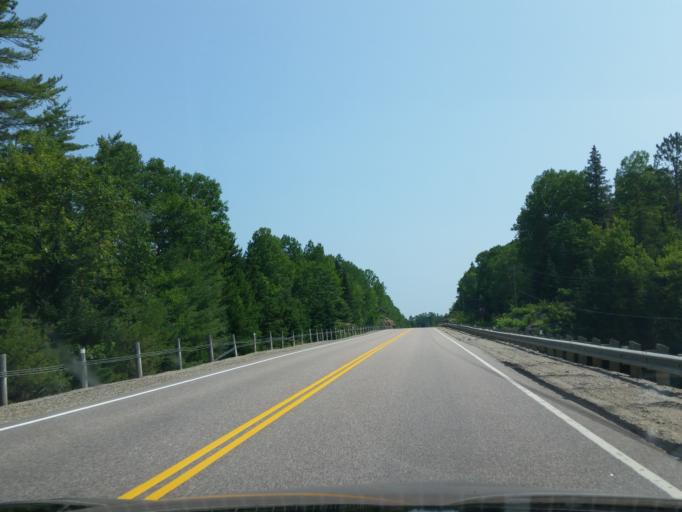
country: CA
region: Ontario
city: Deep River
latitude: 46.1796
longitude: -77.7632
